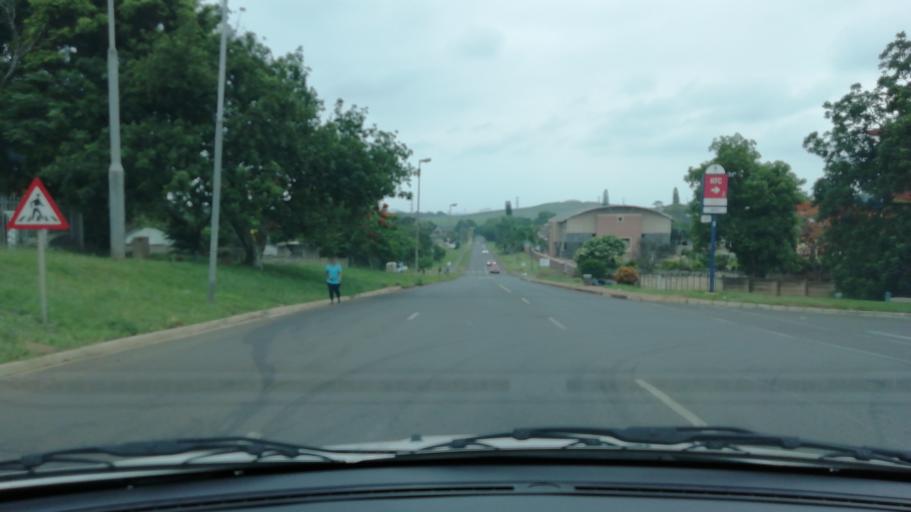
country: ZA
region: KwaZulu-Natal
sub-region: uThungulu District Municipality
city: Empangeni
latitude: -28.7392
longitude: 31.8909
